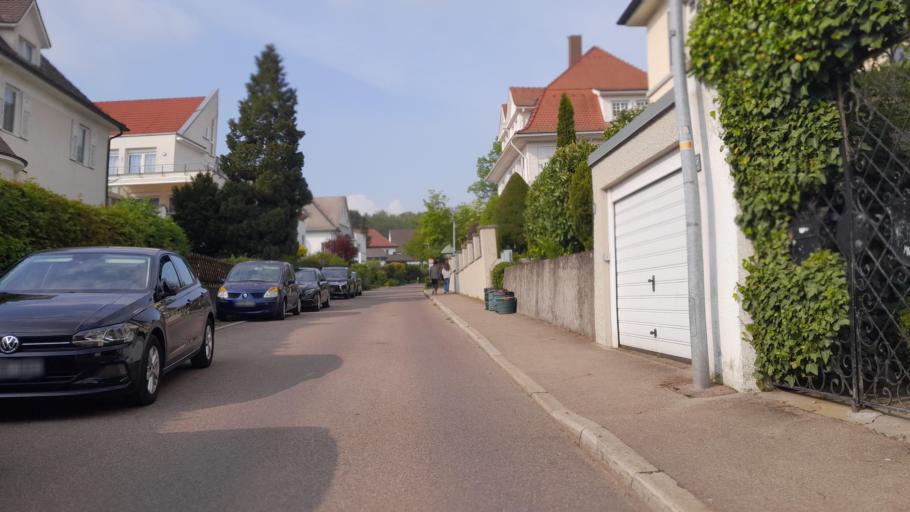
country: DE
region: Baden-Wuerttemberg
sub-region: Regierungsbezirk Stuttgart
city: Goeppingen
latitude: 48.7102
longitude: 9.6600
